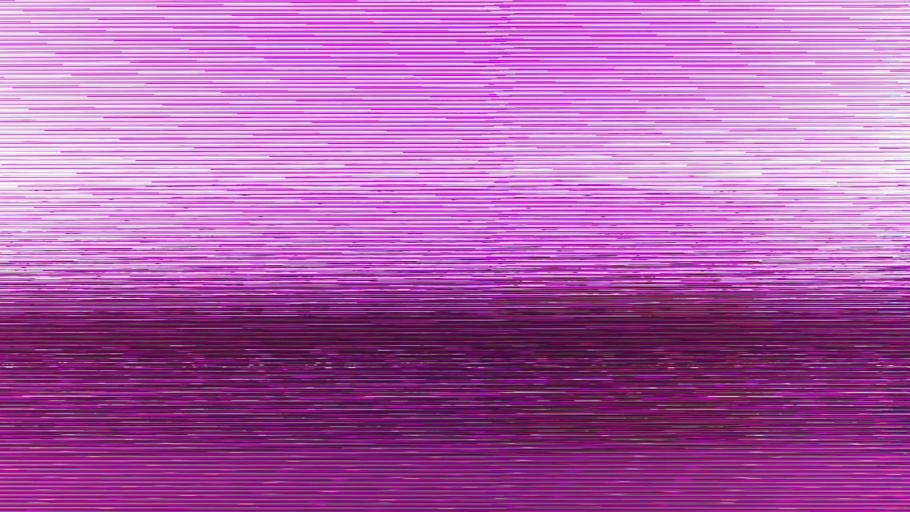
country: US
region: Michigan
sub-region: Washtenaw County
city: Ypsilanti
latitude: 42.2270
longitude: -83.6246
